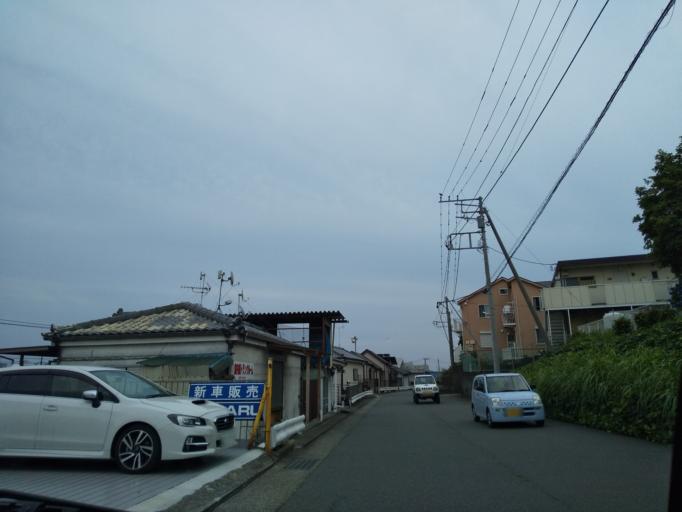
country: JP
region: Kanagawa
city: Atsugi
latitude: 35.4690
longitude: 139.3543
